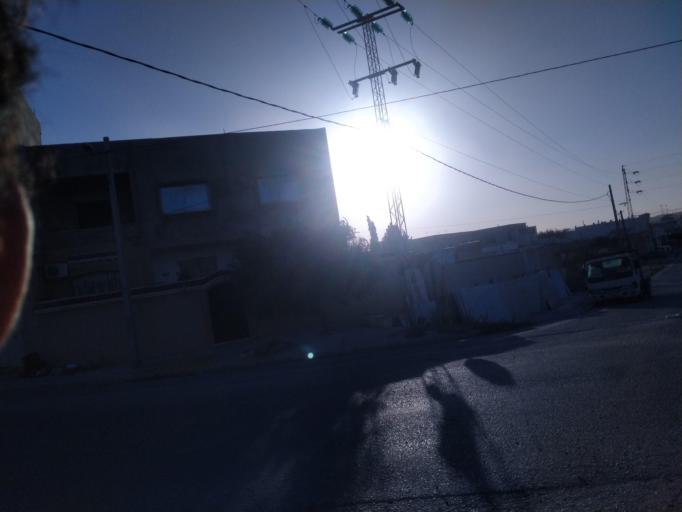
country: TN
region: Susah
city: Akouda
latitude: 35.8174
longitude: 10.5539
